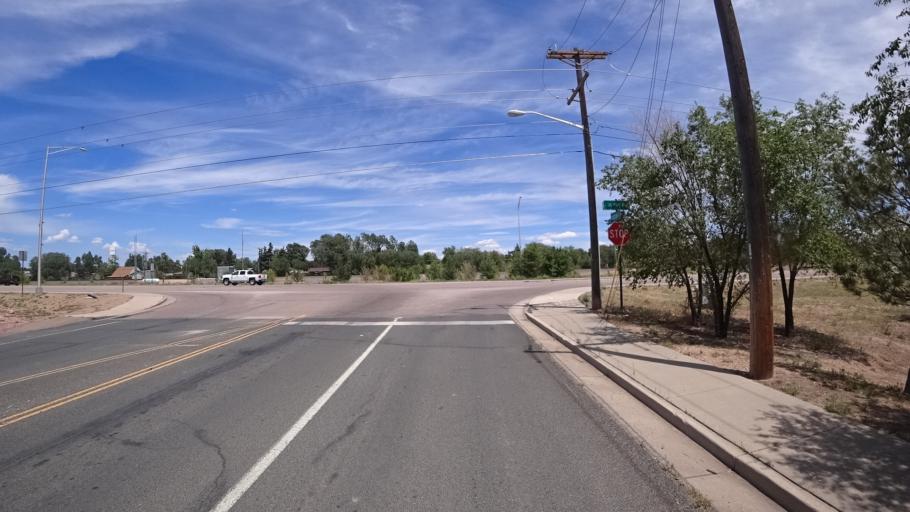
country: US
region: Colorado
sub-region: El Paso County
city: Security-Widefield
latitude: 38.7321
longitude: -104.7269
